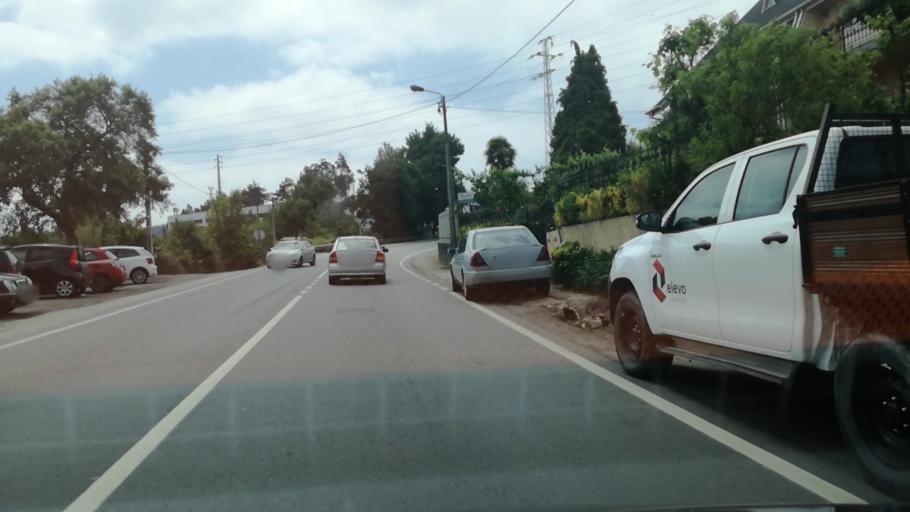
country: PT
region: Porto
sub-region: Trofa
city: Sao Romao do Coronado
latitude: 41.3100
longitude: -8.5808
